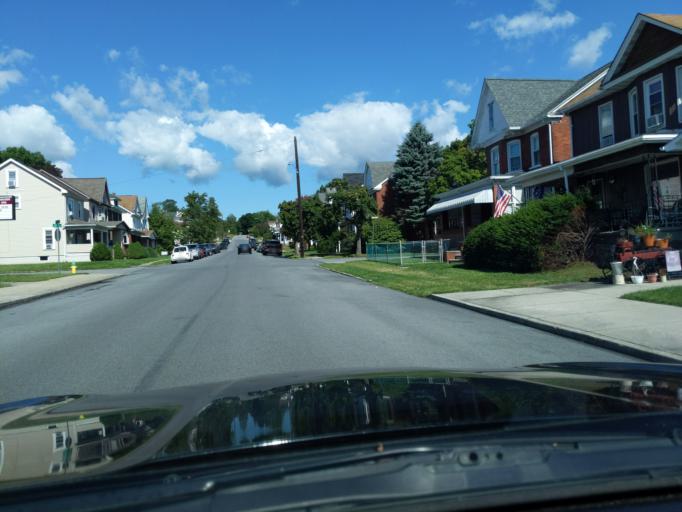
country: US
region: Pennsylvania
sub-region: Blair County
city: Altoona
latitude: 40.5369
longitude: -78.3899
